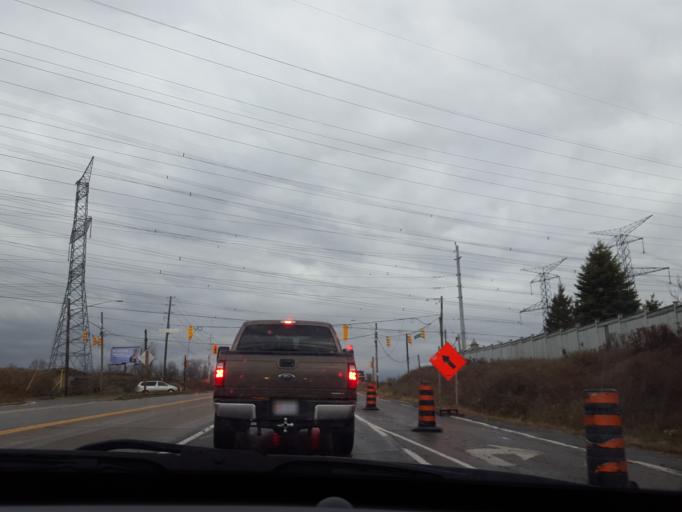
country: CA
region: Ontario
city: Ajax
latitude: 43.8670
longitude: -79.0826
